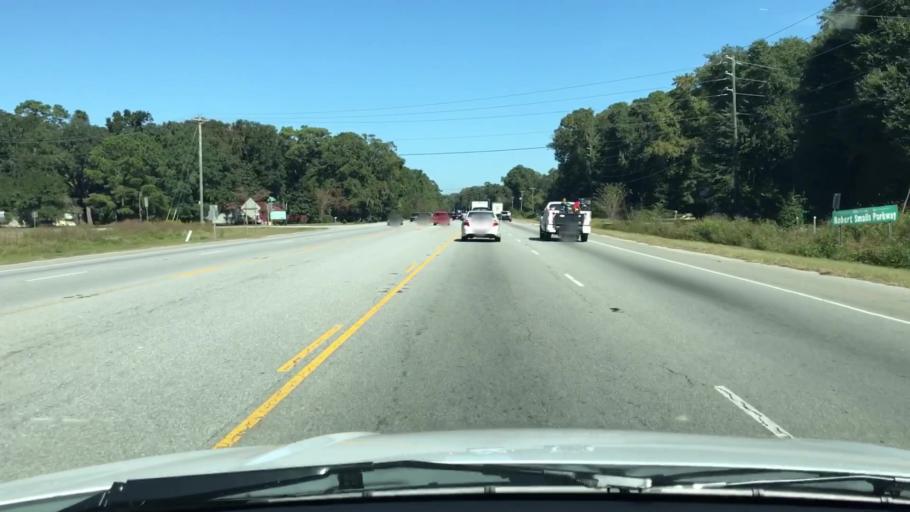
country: US
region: South Carolina
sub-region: Beaufort County
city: Shell Point
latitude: 32.3966
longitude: -80.7660
